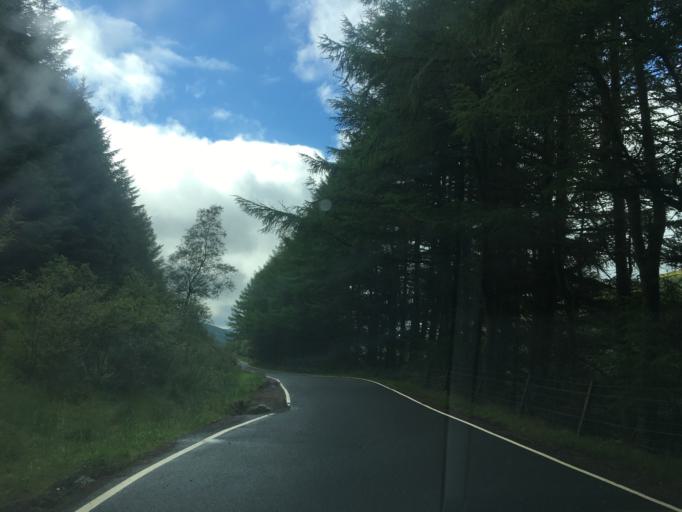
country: GB
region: Scotland
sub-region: Argyll and Bute
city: Port Bannatyne
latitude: 56.0048
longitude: -5.0897
